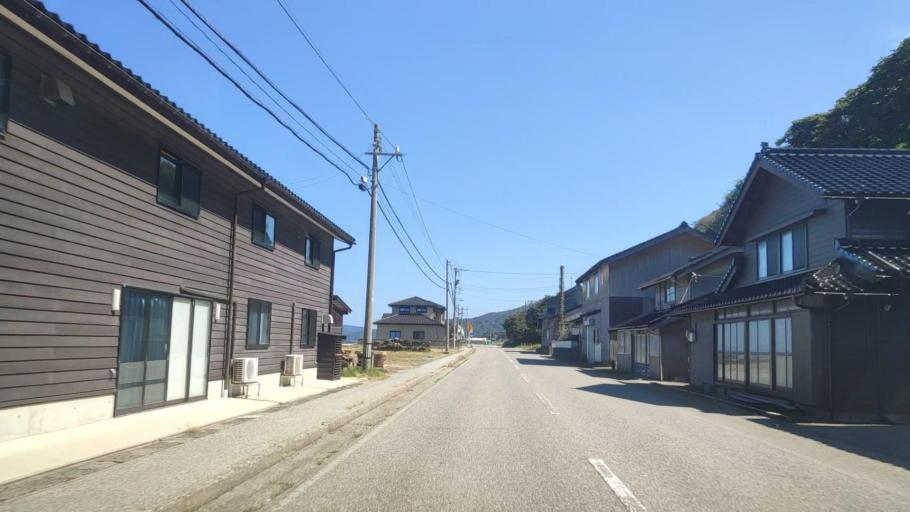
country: JP
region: Ishikawa
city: Nanao
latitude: 37.5022
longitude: 137.1668
